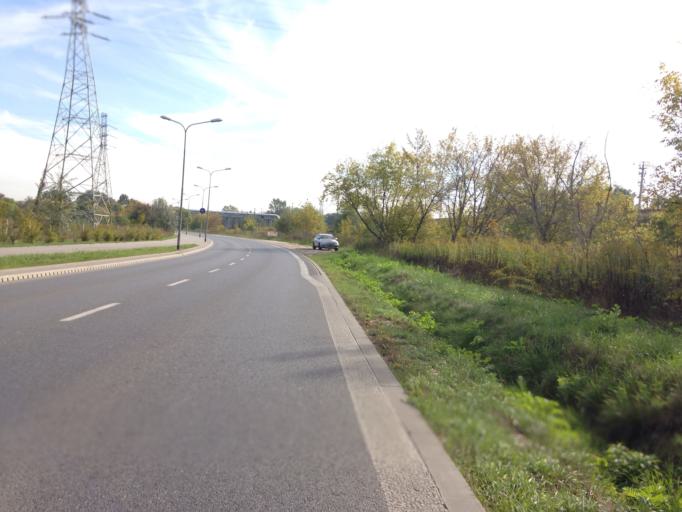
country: PL
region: Masovian Voivodeship
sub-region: Warszawa
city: Praga Poludnie
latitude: 52.2595
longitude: 21.1170
